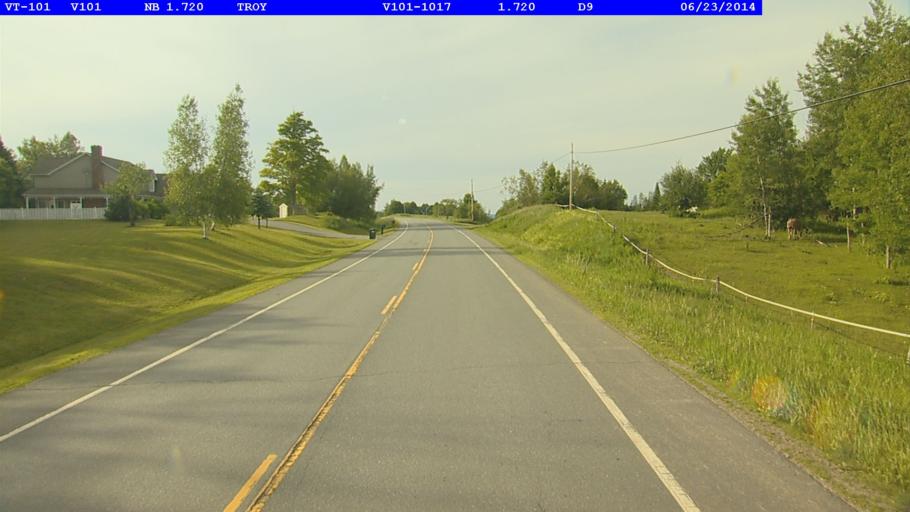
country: US
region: Vermont
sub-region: Orleans County
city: Newport
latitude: 44.9279
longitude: -72.4083
